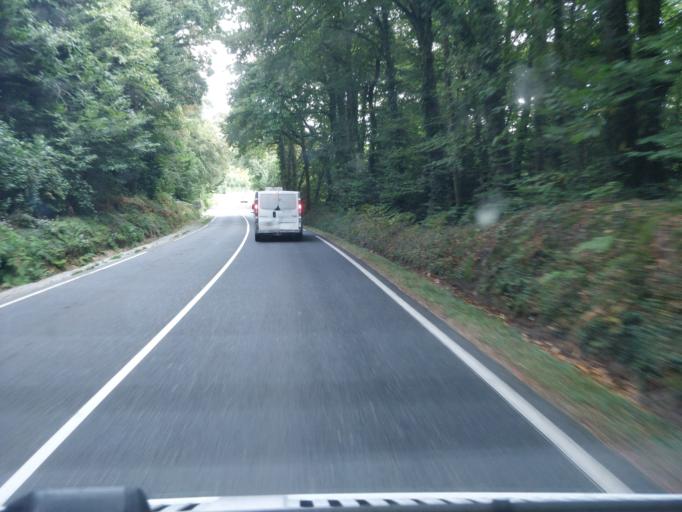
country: FR
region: Brittany
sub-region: Departement du Finistere
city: Pluguffan
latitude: 48.0000
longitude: -4.1598
